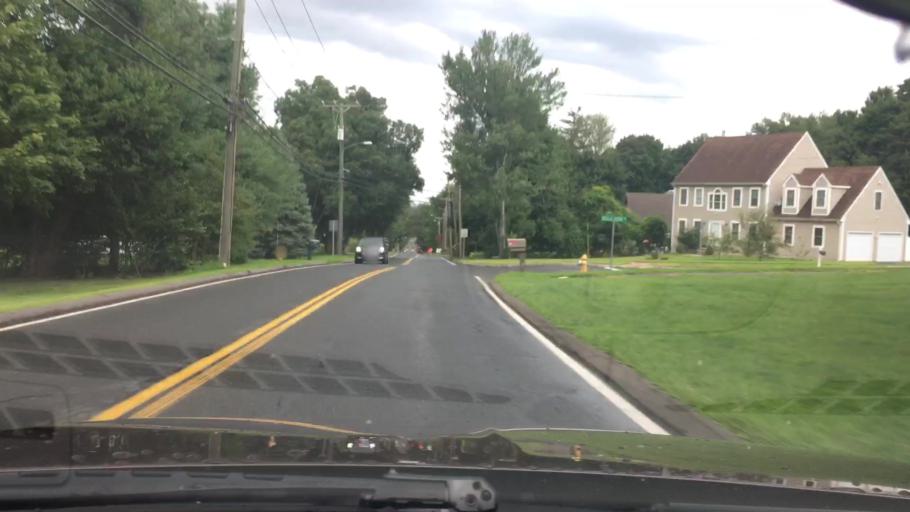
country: US
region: Connecticut
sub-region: Hartford County
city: Manchester
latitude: 41.7476
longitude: -72.5392
